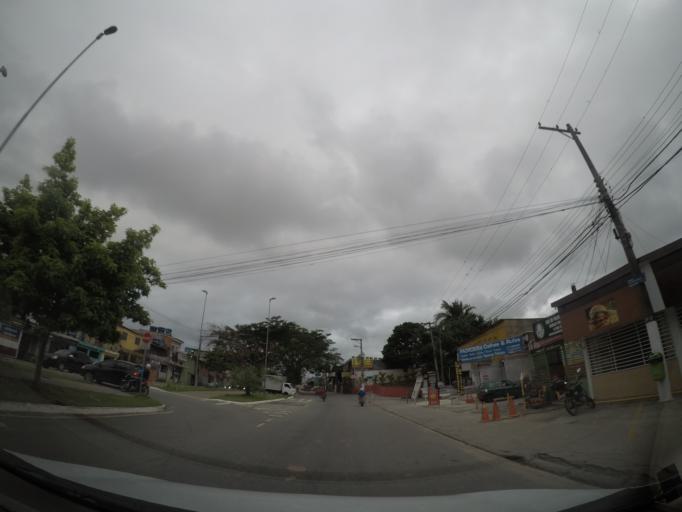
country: BR
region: Sao Paulo
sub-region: Guarulhos
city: Guarulhos
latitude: -23.4082
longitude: -46.4500
